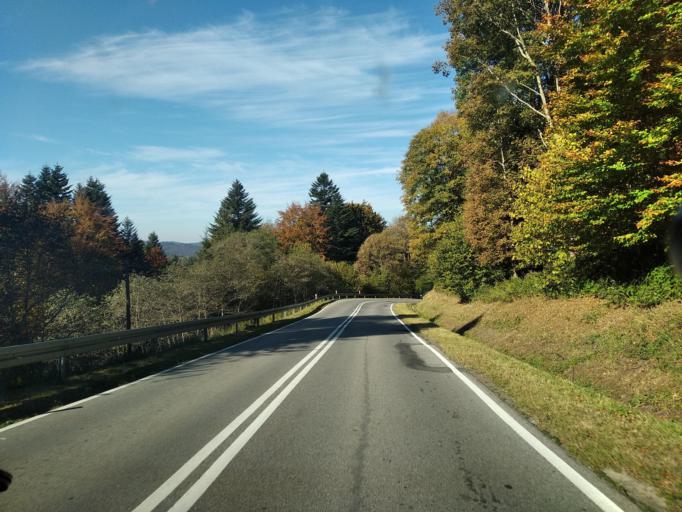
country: PL
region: Subcarpathian Voivodeship
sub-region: Powiat leski
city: Cisna
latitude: 49.2461
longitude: 22.2893
